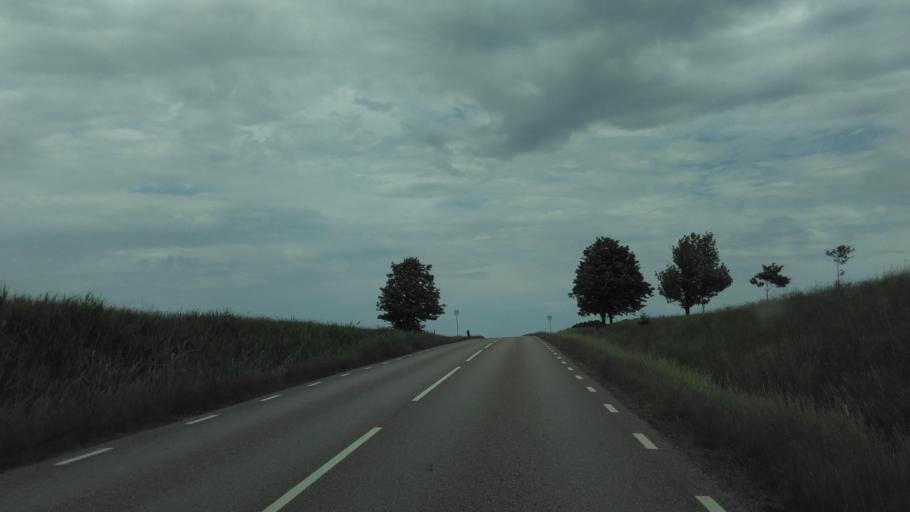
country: SE
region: Vaestra Goetaland
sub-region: Lidkopings Kommun
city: Lidkoping
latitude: 58.4241
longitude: 13.1598
